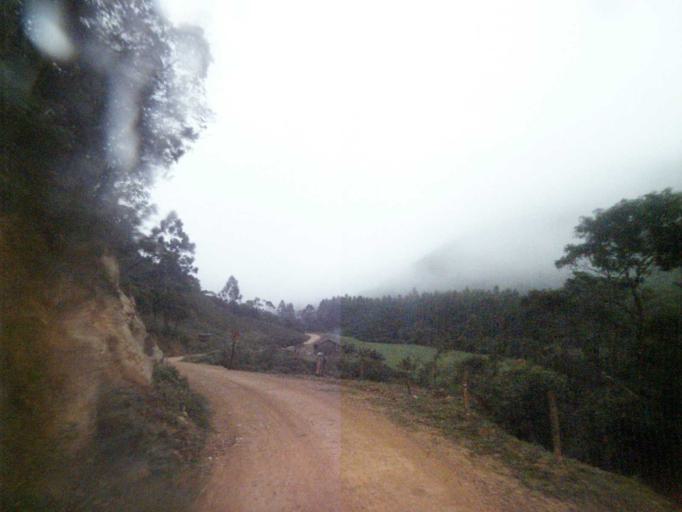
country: BR
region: Santa Catarina
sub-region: Anitapolis
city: Anitapolis
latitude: -27.8081
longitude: -49.1417
